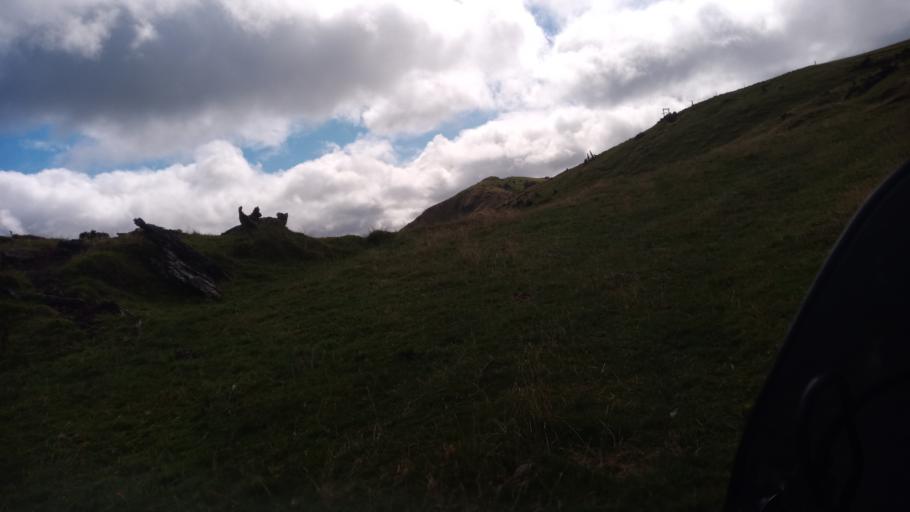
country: NZ
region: Gisborne
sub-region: Gisborne District
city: Gisborne
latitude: -38.4754
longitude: 177.5351
